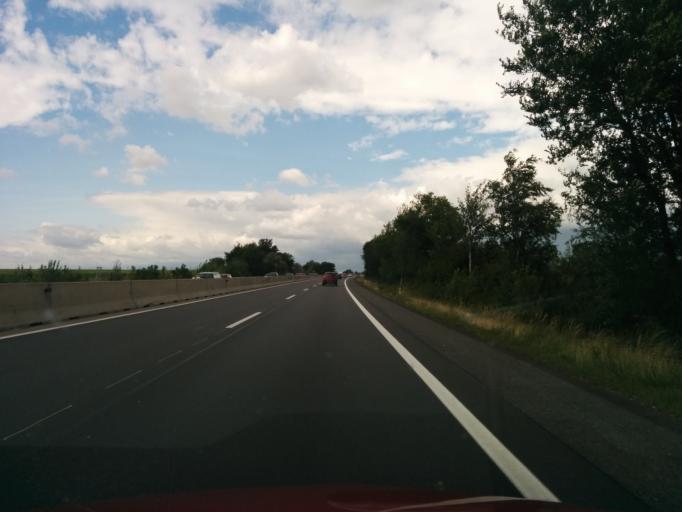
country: AT
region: Lower Austria
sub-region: Politischer Bezirk Wien-Umgebung
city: Fischamend Dorf
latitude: 48.0993
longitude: 16.6526
